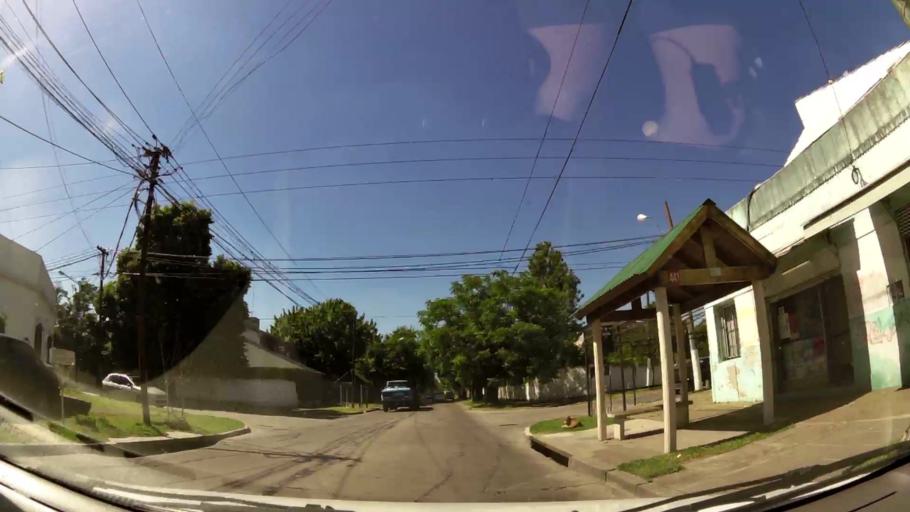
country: AR
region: Buenos Aires
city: Ituzaingo
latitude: -34.6511
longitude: -58.6631
